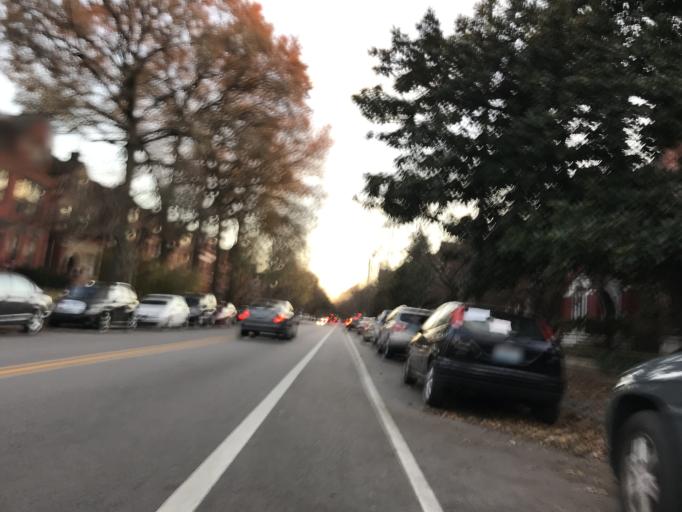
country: US
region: Kentucky
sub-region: Jefferson County
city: Louisville
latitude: 38.2337
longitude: -85.7556
